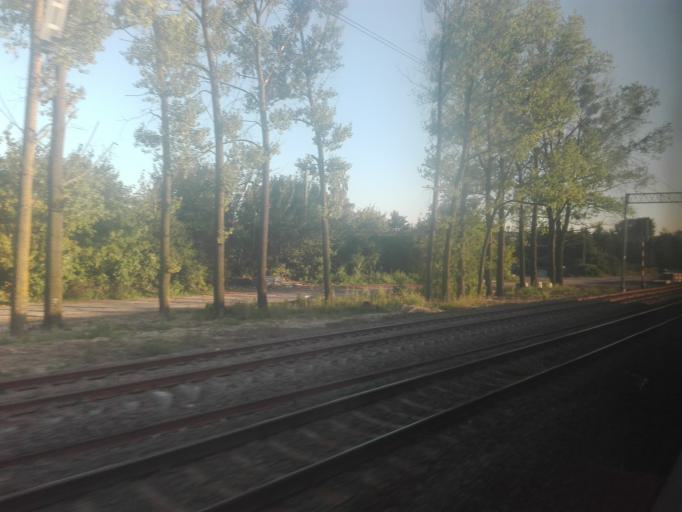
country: PL
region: Masovian Voivodeship
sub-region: Warszawa
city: Ursus
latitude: 52.2049
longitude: 20.9113
